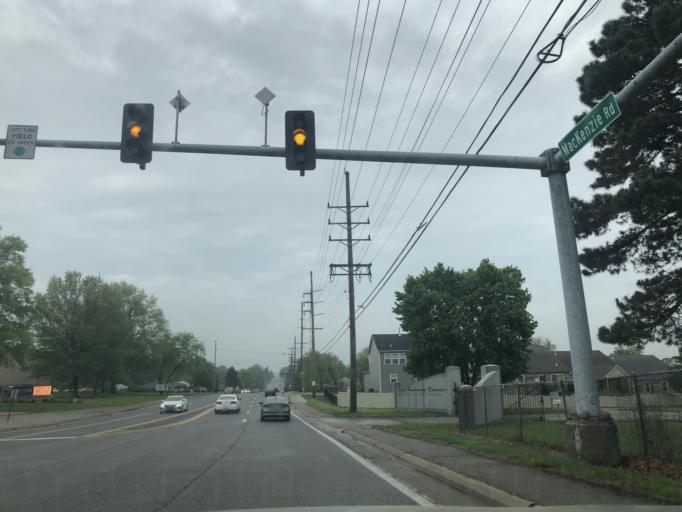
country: US
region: Missouri
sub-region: Saint Louis County
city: Affton
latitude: 38.5587
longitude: -90.3218
